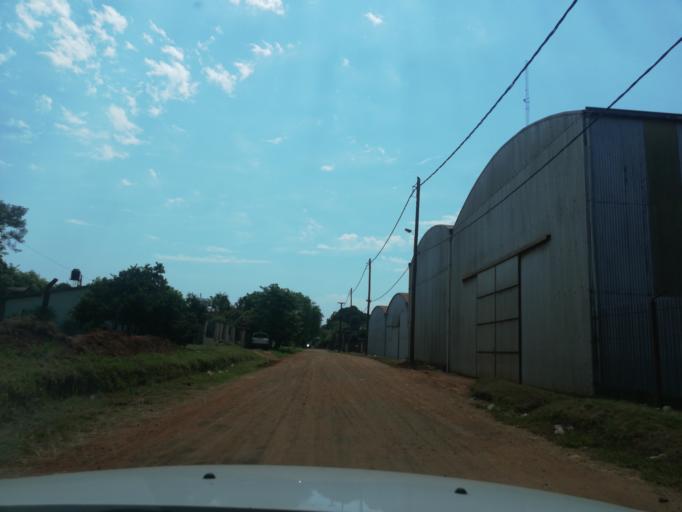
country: AR
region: Misiones
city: Garupa
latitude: -27.4399
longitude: -55.8864
